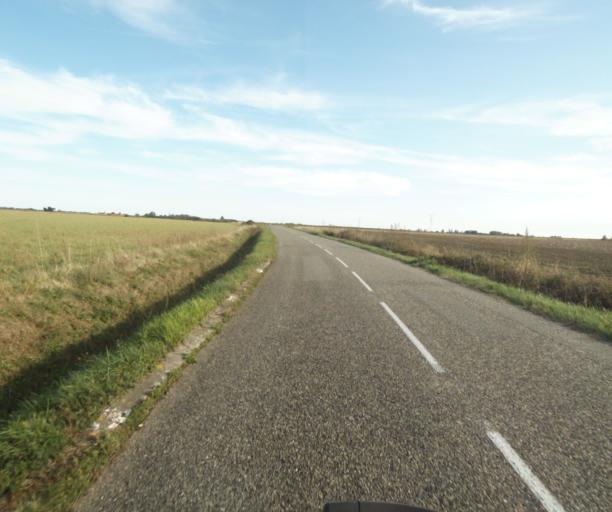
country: FR
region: Midi-Pyrenees
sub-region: Departement du Tarn-et-Garonne
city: Finhan
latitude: 43.9095
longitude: 1.1147
